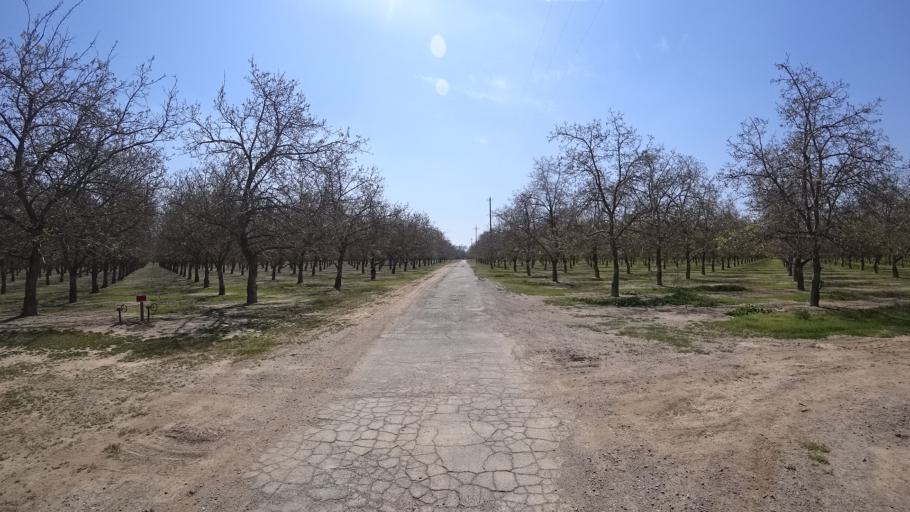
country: US
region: California
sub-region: Glenn County
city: Willows
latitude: 39.4929
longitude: -122.0122
